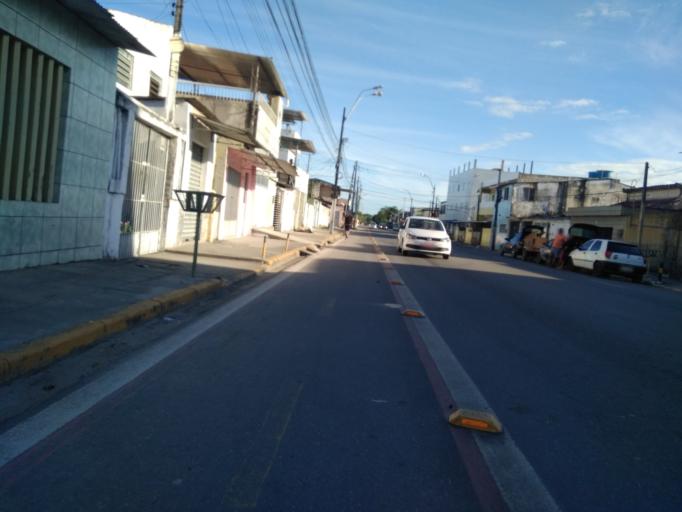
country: BR
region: Pernambuco
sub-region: Recife
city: Recife
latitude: -8.0737
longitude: -34.9297
